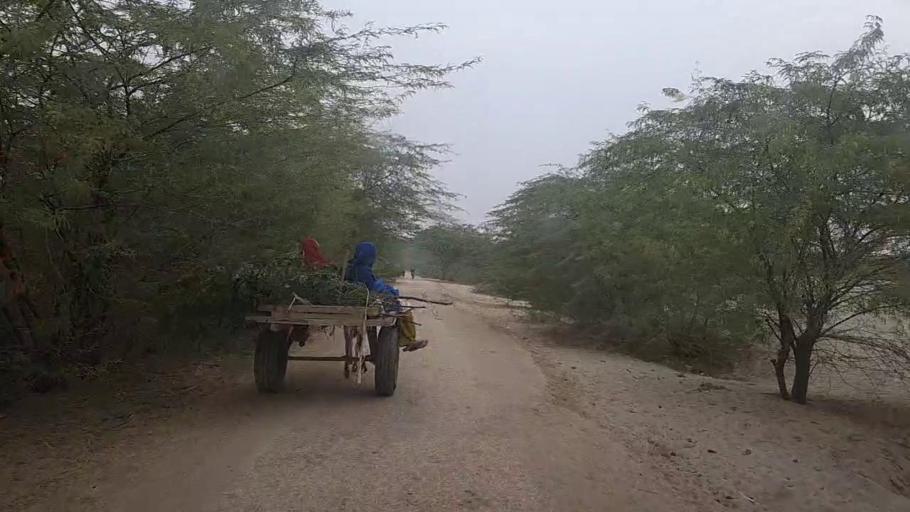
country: PK
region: Sindh
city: Gambat
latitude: 27.3526
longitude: 68.5995
